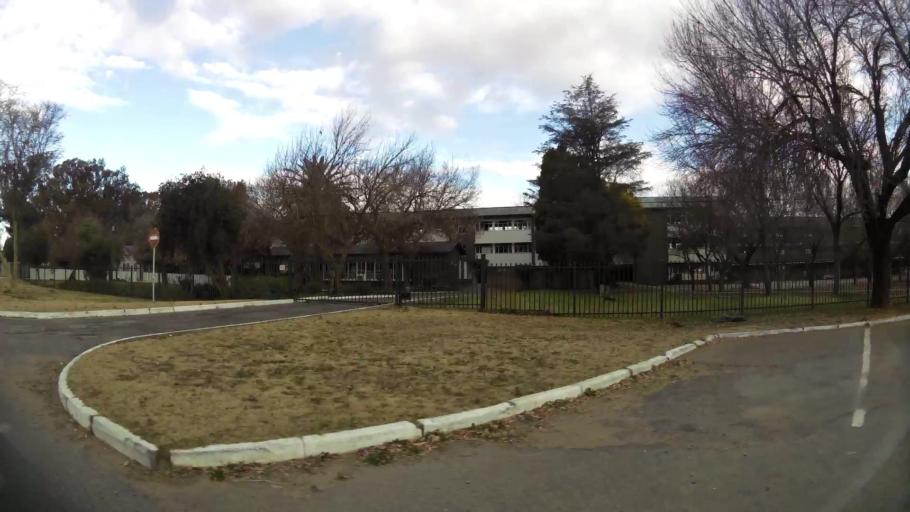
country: ZA
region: Orange Free State
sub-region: Lejweleputswa District Municipality
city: Welkom
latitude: -27.9945
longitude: 26.7081
